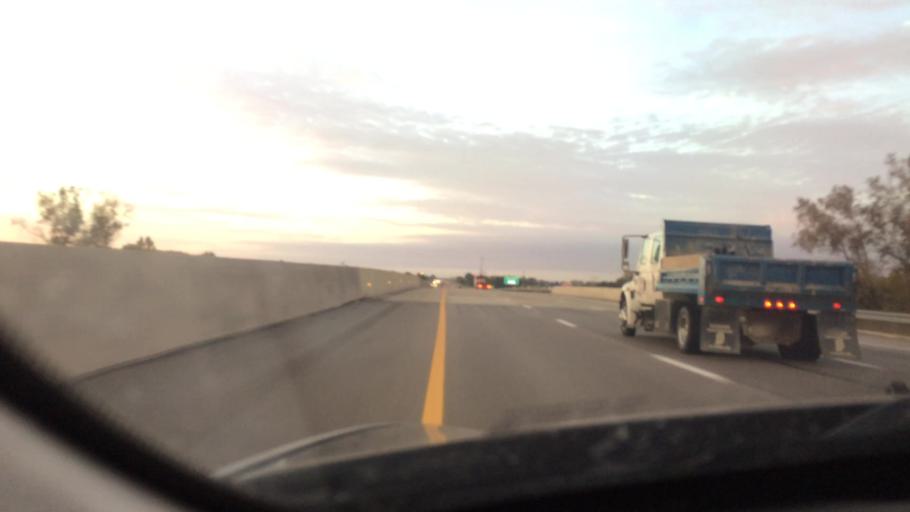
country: US
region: Ohio
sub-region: Hancock County
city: Findlay
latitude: 41.1111
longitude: -83.6599
